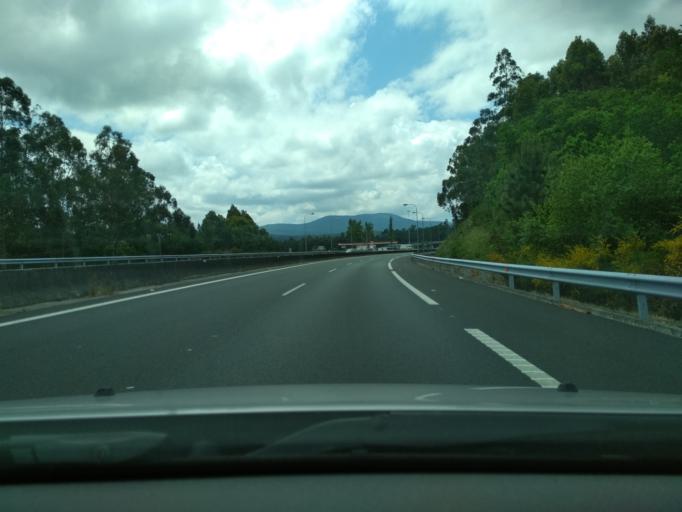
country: ES
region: Galicia
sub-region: Provincia de Pontevedra
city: Portas
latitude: 42.5665
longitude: -8.6707
